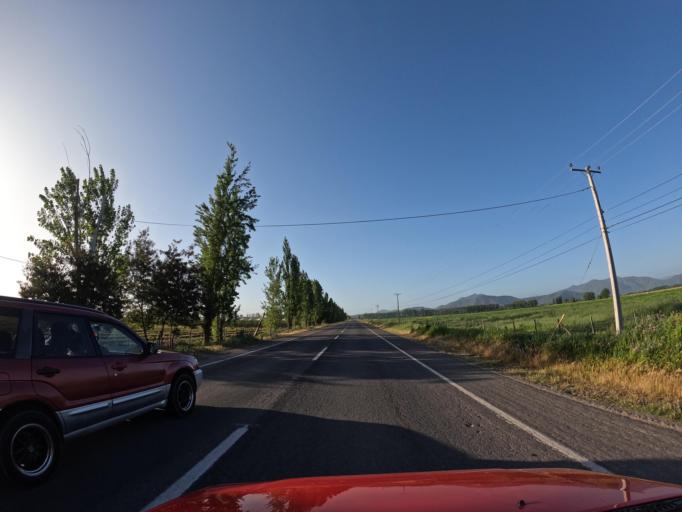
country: CL
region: O'Higgins
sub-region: Provincia de Colchagua
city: Santa Cruz
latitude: -34.4667
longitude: -71.3625
